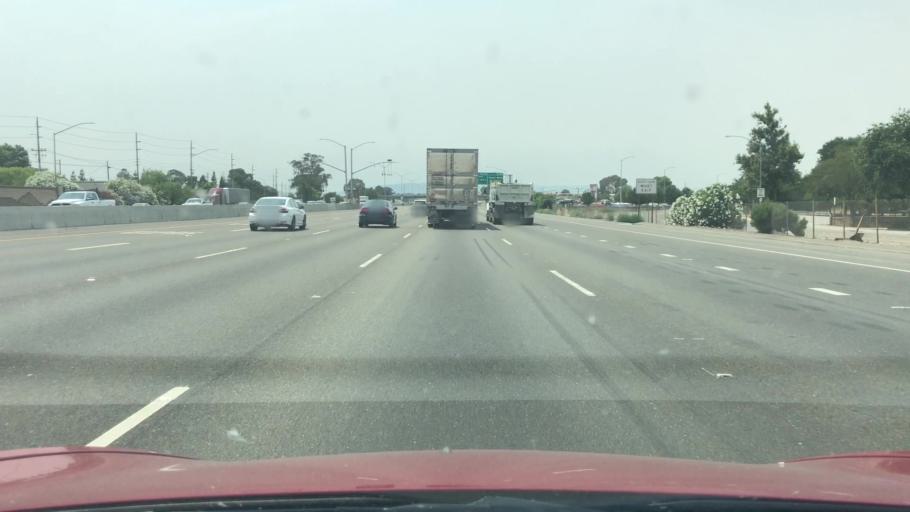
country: US
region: California
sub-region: Alameda County
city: Livermore
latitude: 37.7120
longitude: -121.7176
